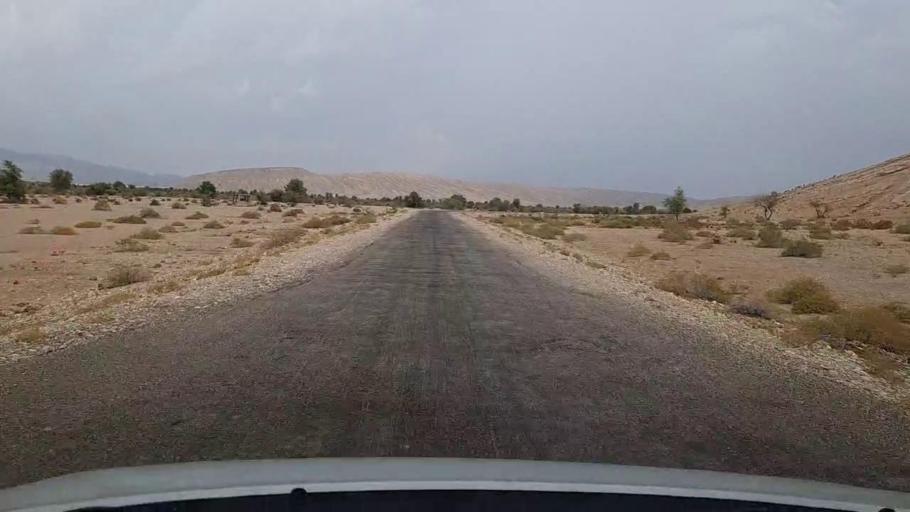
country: PK
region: Sindh
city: Sehwan
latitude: 26.2243
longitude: 67.7119
